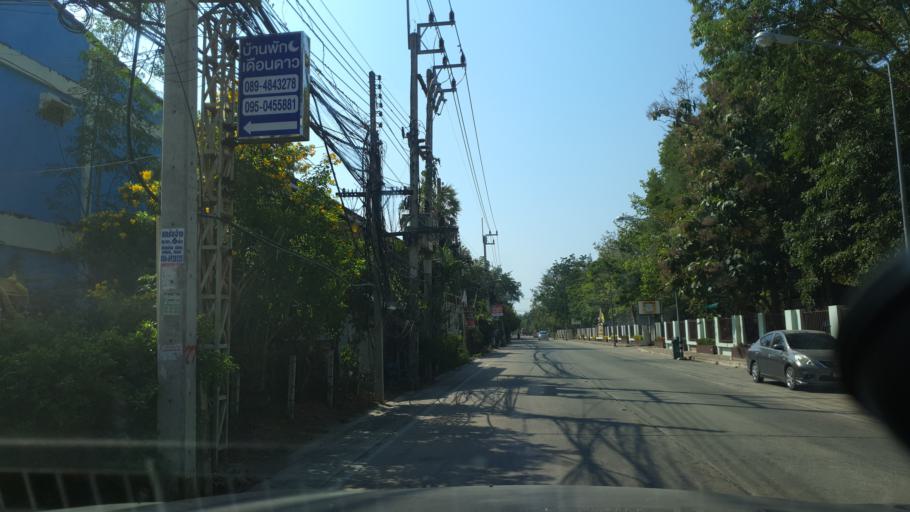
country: TH
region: Phetchaburi
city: Cha-am
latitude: 12.8007
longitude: 99.9842
